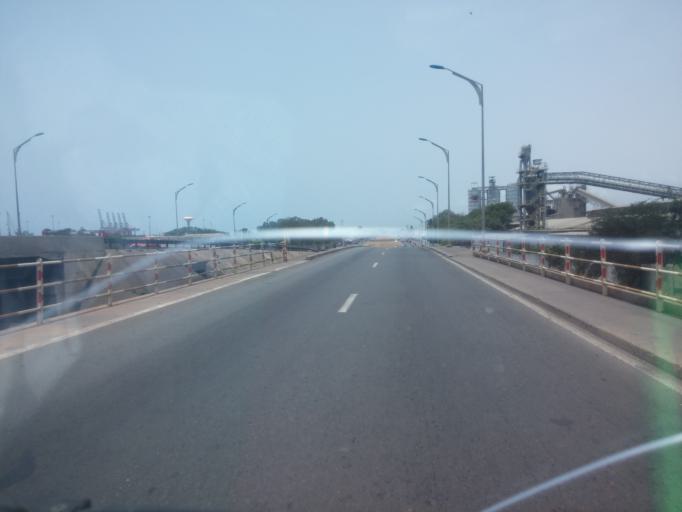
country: TG
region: Maritime
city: Lome
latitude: 6.1526
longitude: 1.2907
